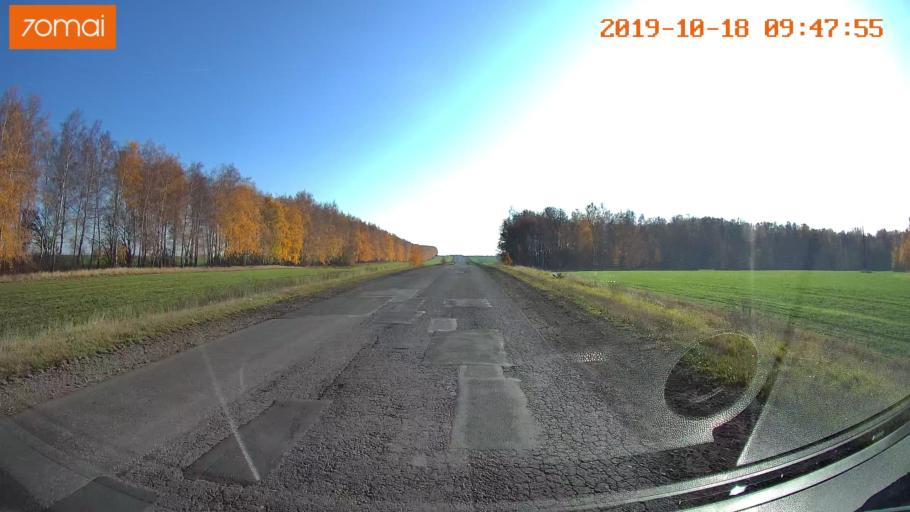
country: RU
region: Tula
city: Kazachka
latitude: 53.3200
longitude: 38.2387
